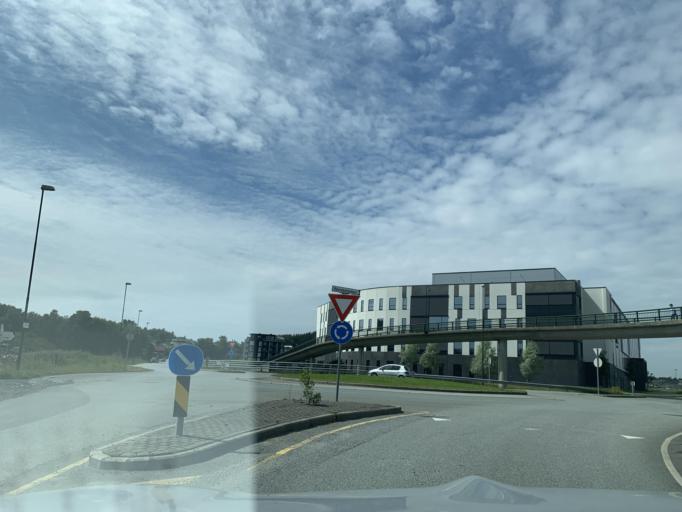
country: NO
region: Rogaland
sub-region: Sola
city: Sola
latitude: 58.8938
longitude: 5.6822
